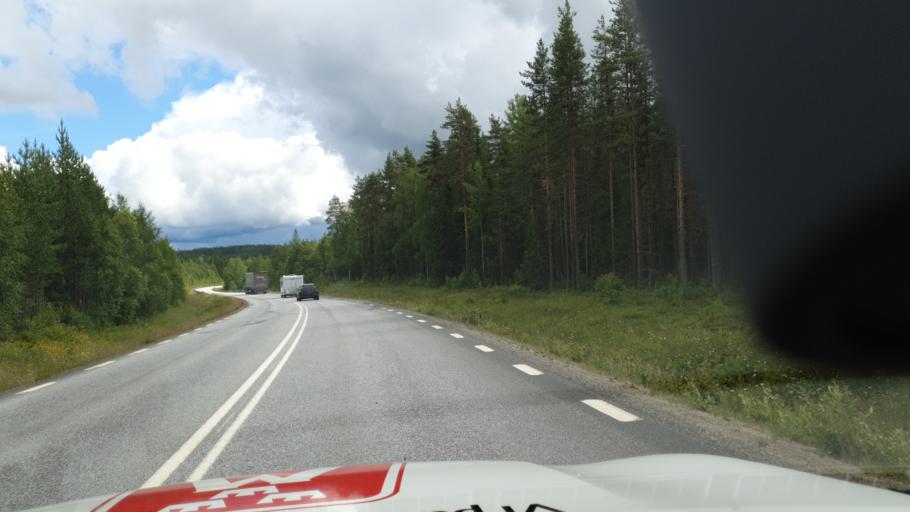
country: SE
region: Vaesterbotten
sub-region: Vannas Kommun
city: Vaennaes
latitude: 63.9478
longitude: 19.7597
